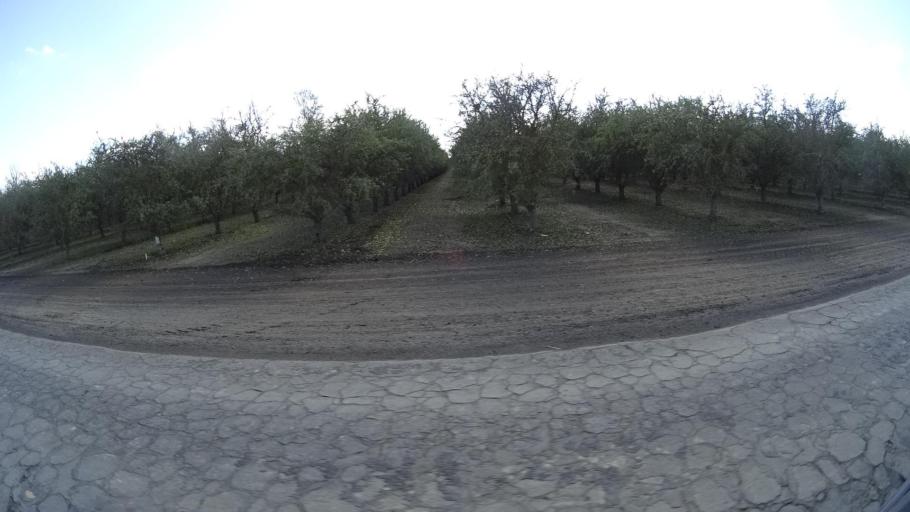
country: US
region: California
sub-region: Kern County
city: Delano
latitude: 35.7322
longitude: -119.3557
